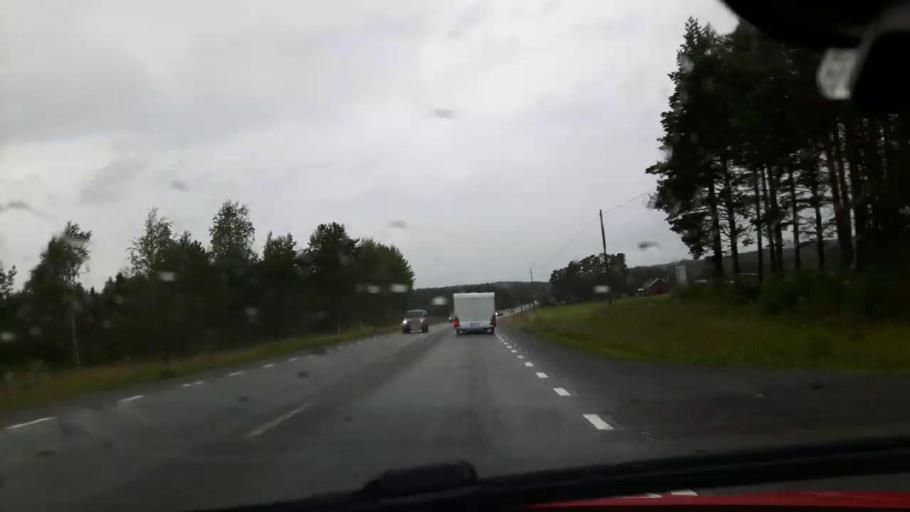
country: SE
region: Jaemtland
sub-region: Are Kommun
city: Jarpen
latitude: 63.3292
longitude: 13.5298
